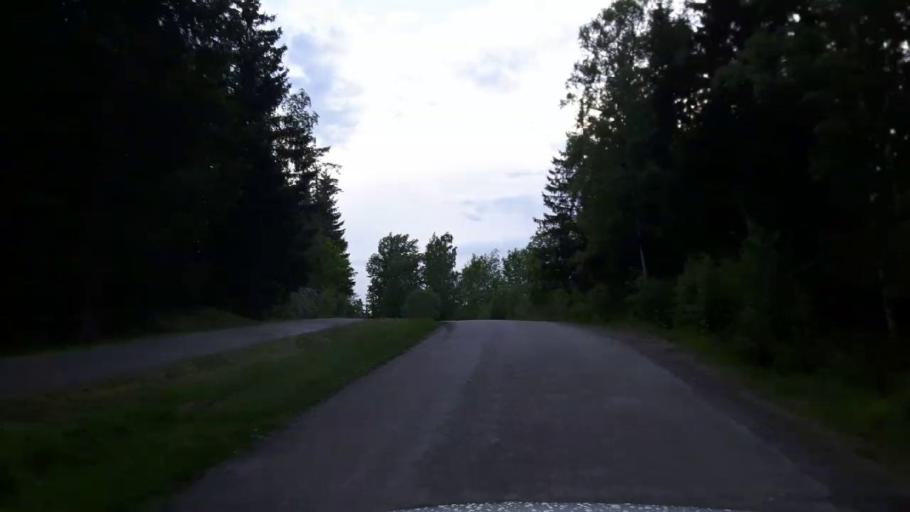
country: SE
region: Stockholm
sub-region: Upplands-Bro Kommun
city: Bro
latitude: 59.5209
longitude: 17.6717
